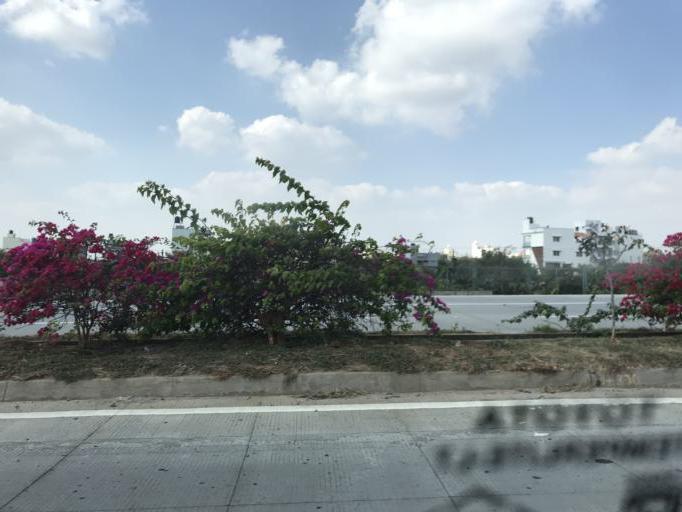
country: IN
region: Karnataka
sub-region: Bangalore Urban
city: Bangalore
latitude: 12.8824
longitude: 77.4991
